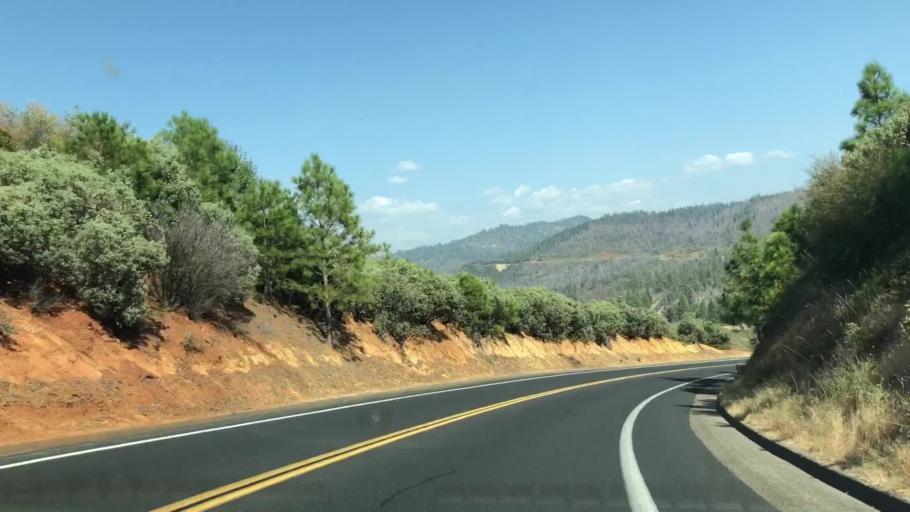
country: US
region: California
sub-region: Tuolumne County
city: Tuolumne City
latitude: 37.8252
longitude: -120.0201
